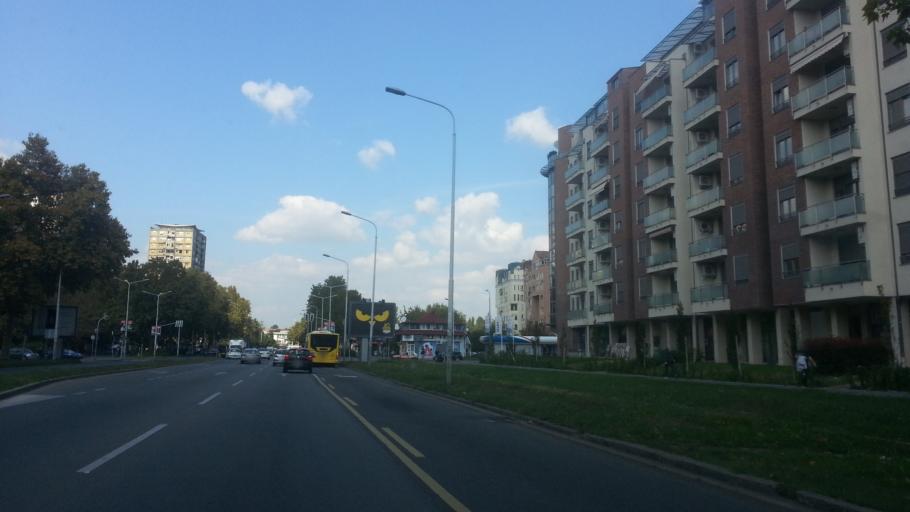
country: RS
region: Central Serbia
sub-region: Belgrade
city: Zemun
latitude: 44.8324
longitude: 20.4105
